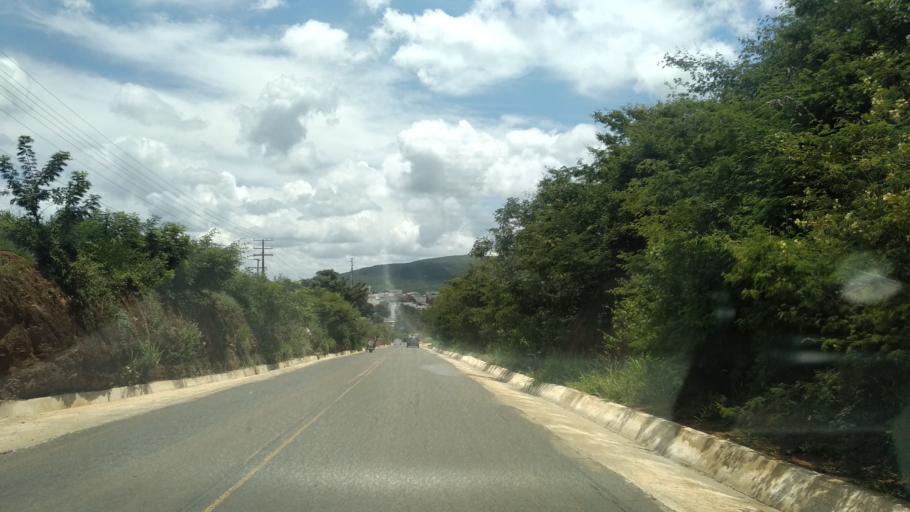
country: BR
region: Bahia
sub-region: Caetite
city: Caetite
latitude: -14.0587
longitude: -42.4922
